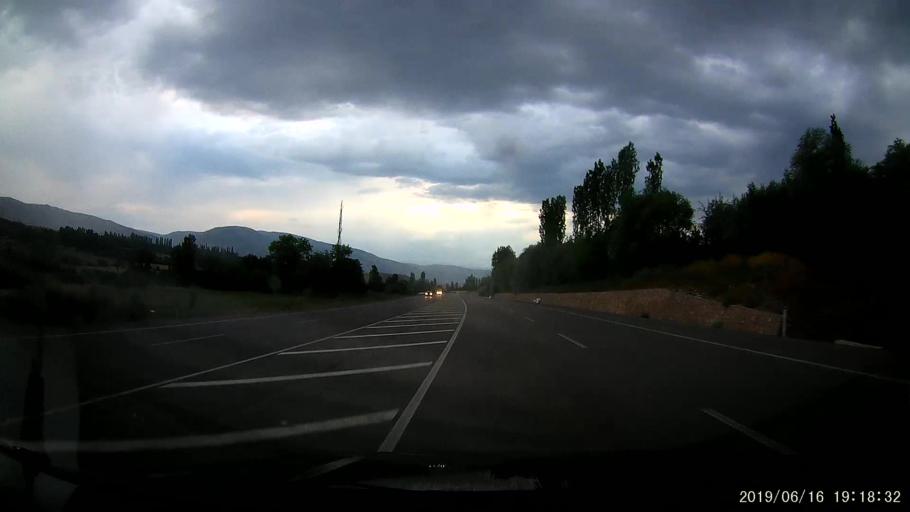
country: TR
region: Sivas
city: Akincilar
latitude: 40.0953
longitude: 38.4550
